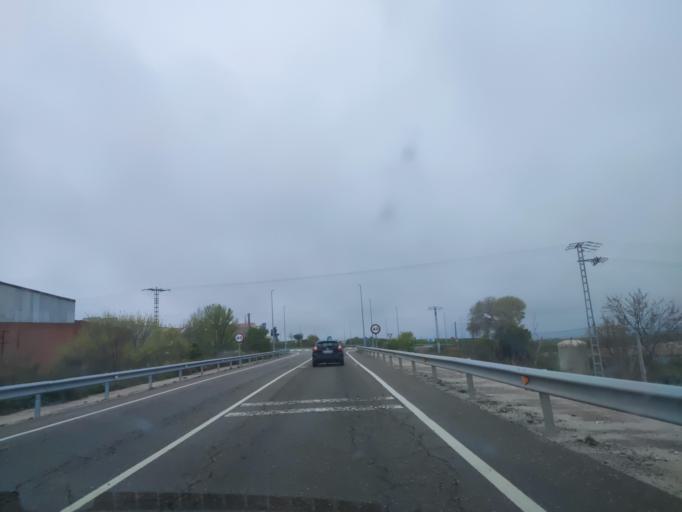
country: ES
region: Castille-La Mancha
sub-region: Province of Toledo
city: Bargas
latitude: 39.9464
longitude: -4.0187
